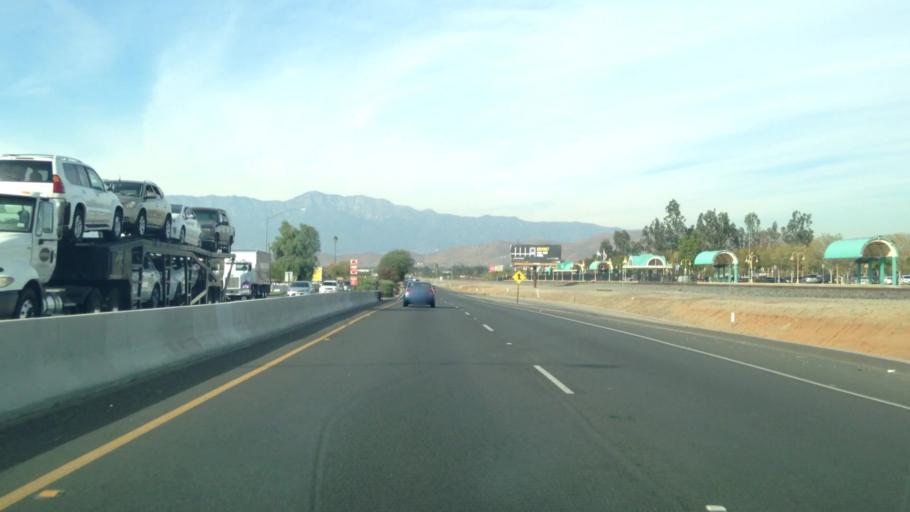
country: US
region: California
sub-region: Riverside County
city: Pedley
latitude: 33.9762
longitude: -117.4762
